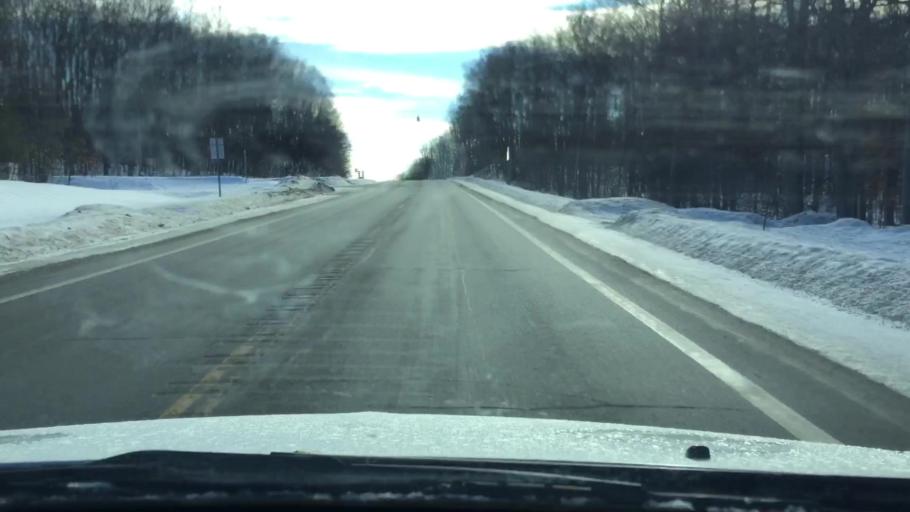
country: US
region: Michigan
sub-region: Antrim County
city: Mancelona
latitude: 44.9757
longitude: -85.0547
